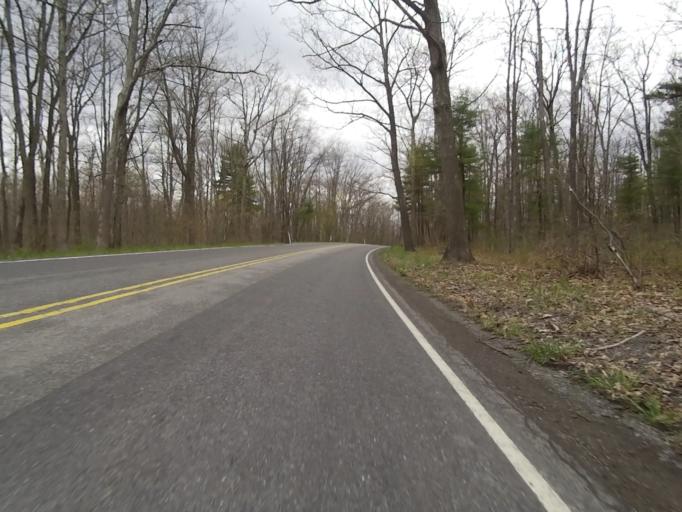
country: US
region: Pennsylvania
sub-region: Centre County
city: Stormstown
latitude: 40.9084
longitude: -78.0824
